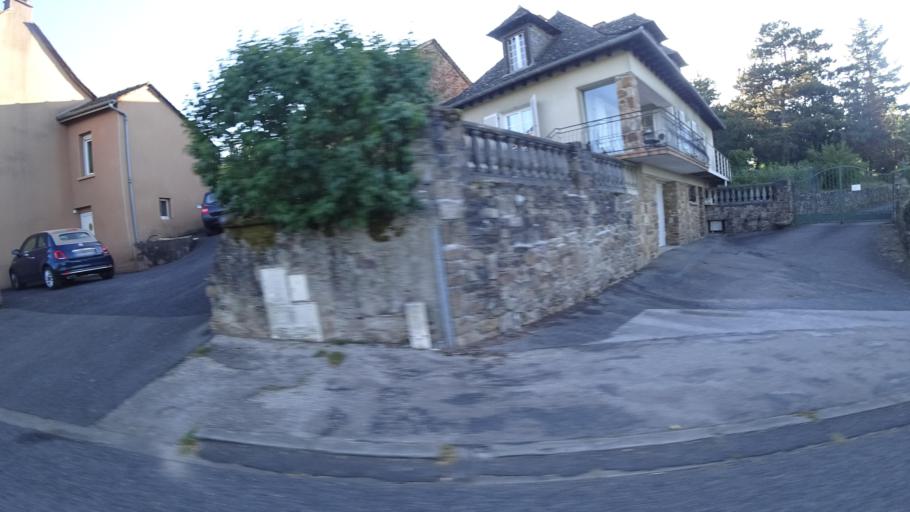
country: FR
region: Midi-Pyrenees
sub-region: Departement de l'Aveyron
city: Olemps
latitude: 44.3323
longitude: 2.5596
